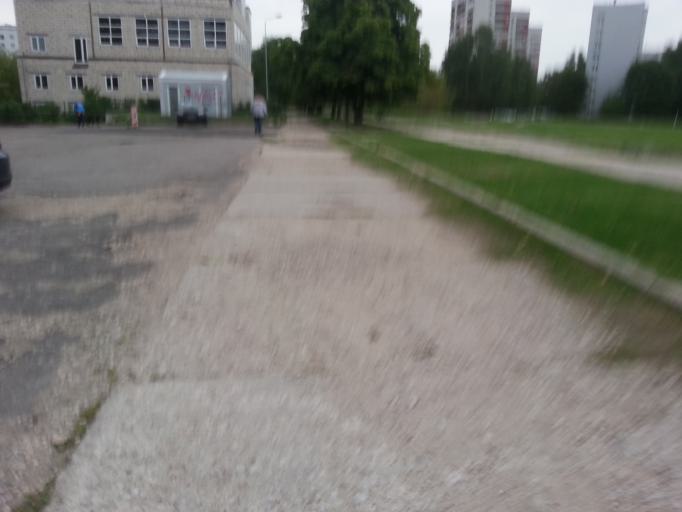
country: LV
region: Stopini
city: Ulbroka
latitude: 56.9646
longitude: 24.2353
